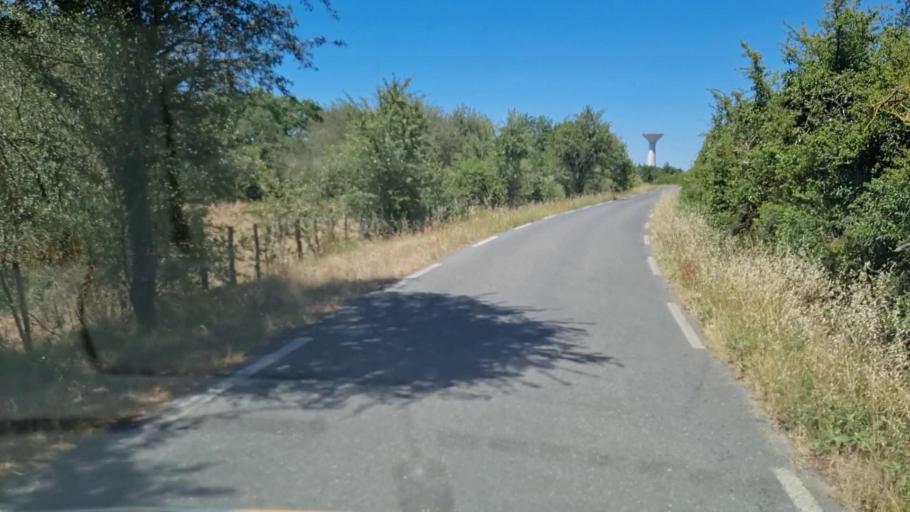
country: FR
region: Languedoc-Roussillon
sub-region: Departement du Gard
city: Le Cailar
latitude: 43.6299
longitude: 4.2509
